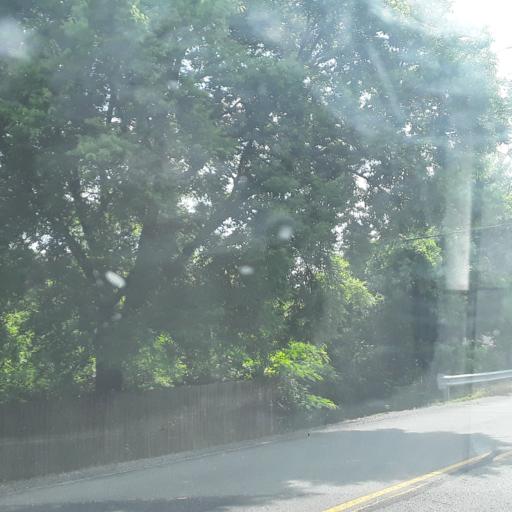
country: US
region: Tennessee
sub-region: Davidson County
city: Oak Hill
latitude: 36.1154
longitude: -86.7217
